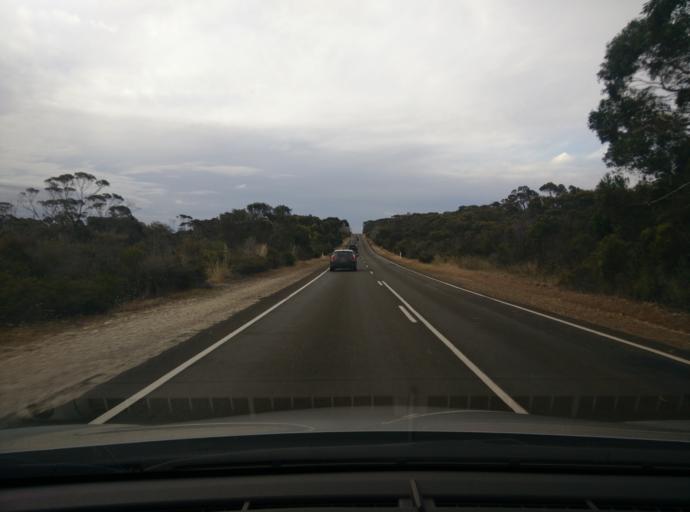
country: AU
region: South Australia
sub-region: Kangaroo Island
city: Kingscote
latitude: -35.7683
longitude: 137.6199
